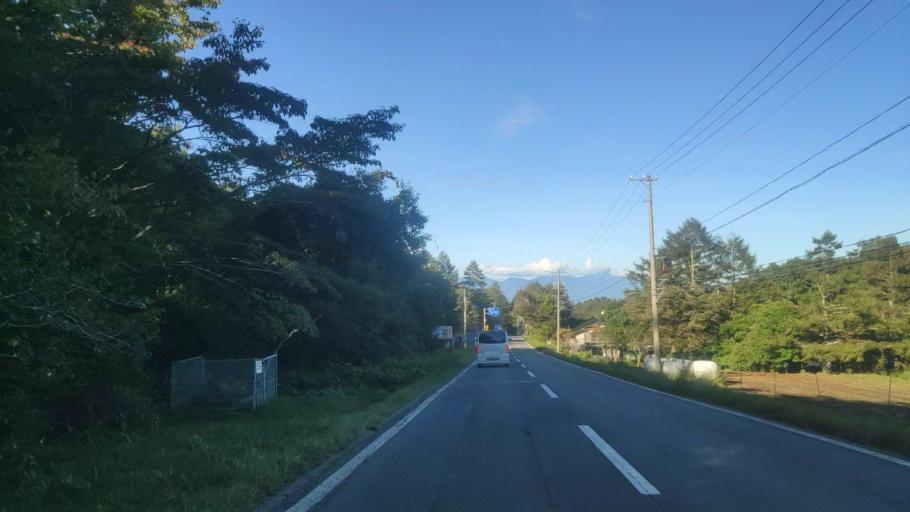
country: JP
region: Nagano
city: Kamimaruko
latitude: 36.1804
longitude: 138.2832
